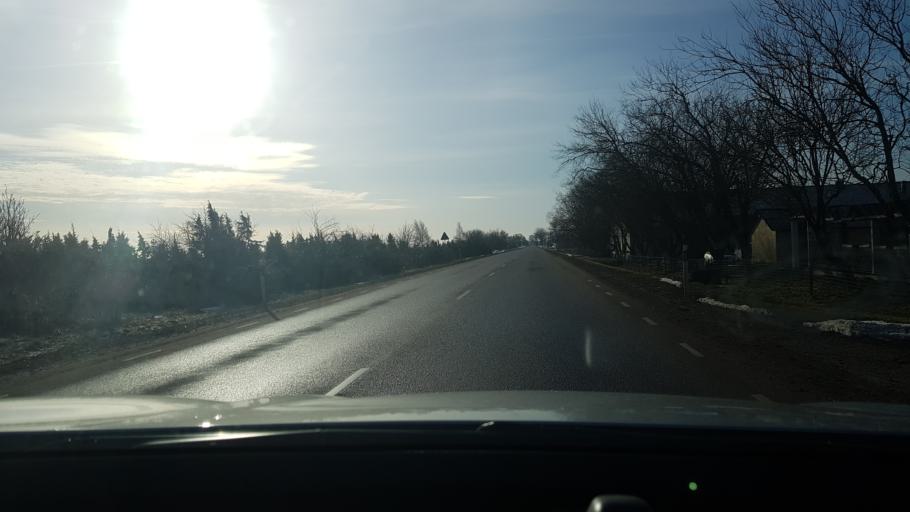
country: EE
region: Saare
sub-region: Kuressaare linn
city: Kuressaare
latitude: 58.2269
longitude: 22.5056
